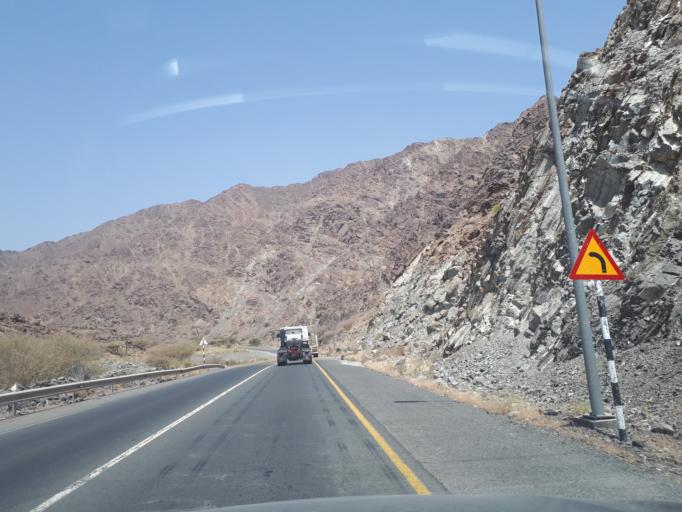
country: OM
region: Muhafazat ad Dakhiliyah
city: Sufalat Sama'il
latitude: 23.2495
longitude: 58.0936
